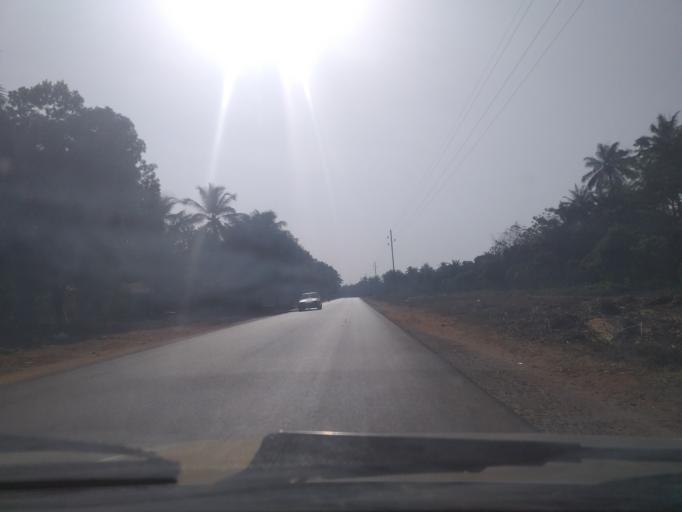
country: GN
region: Boke
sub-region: Boke Prefecture
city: Sangueya
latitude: 10.7782
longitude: -14.4416
